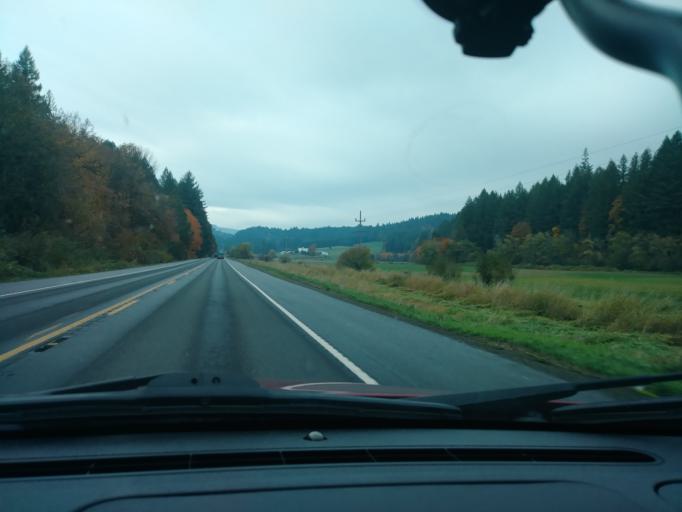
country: US
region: Oregon
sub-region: Washington County
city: Banks
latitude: 45.6142
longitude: -123.1692
